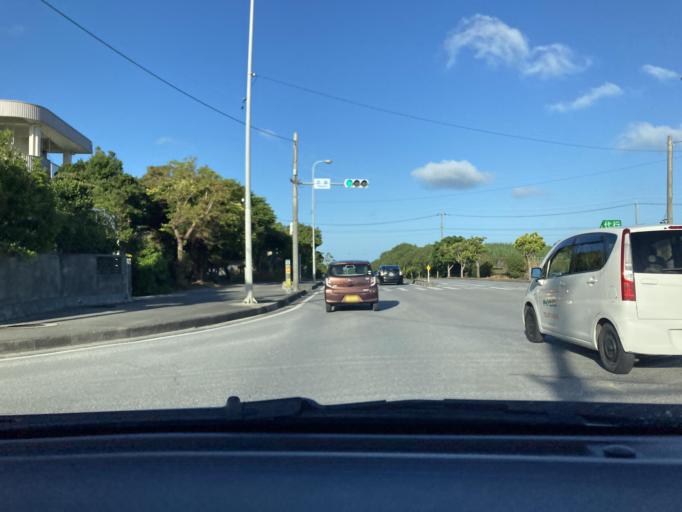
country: JP
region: Okinawa
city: Tomigusuku
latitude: 26.1632
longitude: 127.7048
